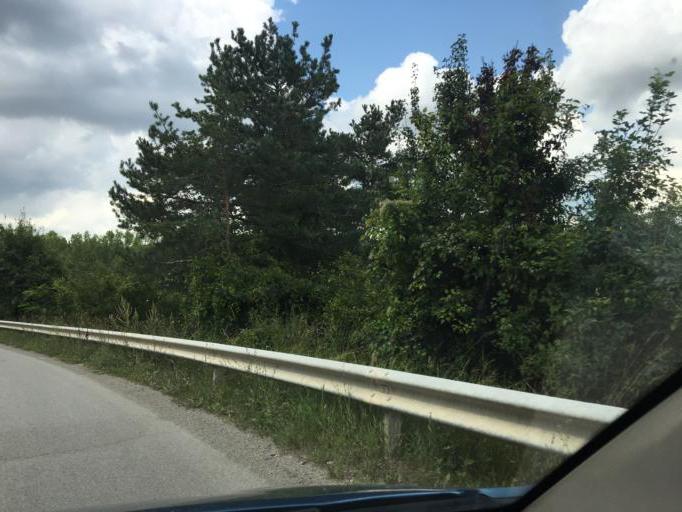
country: BG
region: Sofia-Capital
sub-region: Stolichna Obshtina
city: Sofia
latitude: 42.5939
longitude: 23.3666
